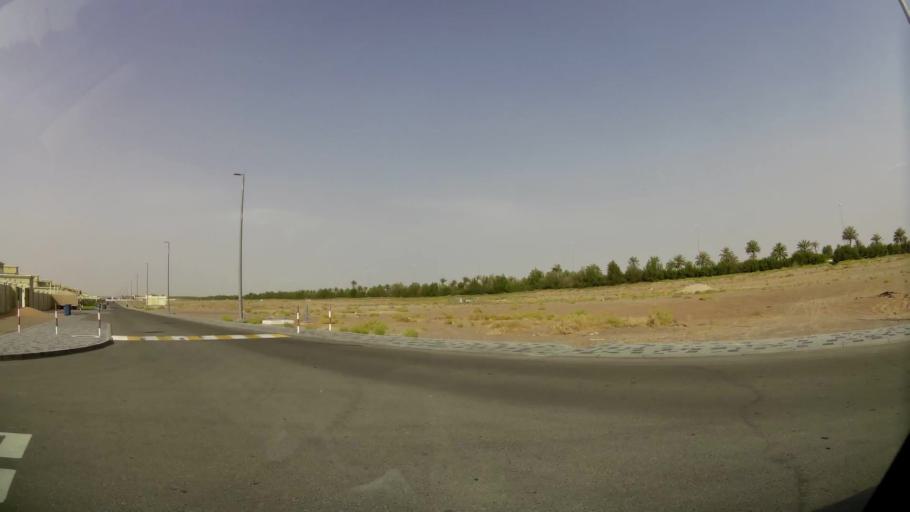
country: AE
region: Abu Dhabi
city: Al Ain
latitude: 24.2059
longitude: 55.5956
